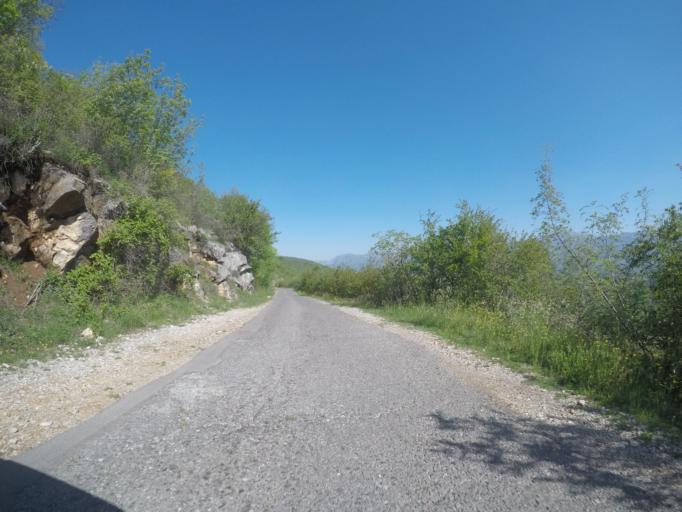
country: ME
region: Danilovgrad
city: Danilovgrad
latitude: 42.5174
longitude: 19.0976
